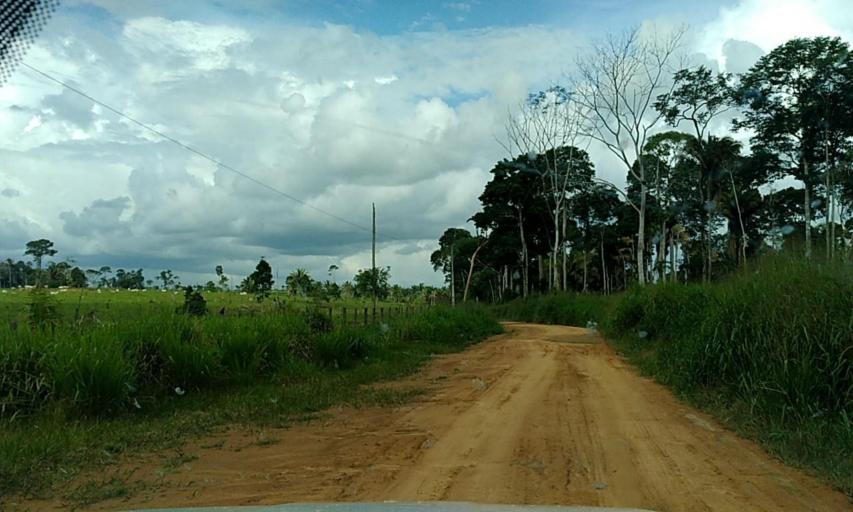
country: BR
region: Para
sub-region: Altamira
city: Altamira
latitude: -3.2336
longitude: -52.7347
